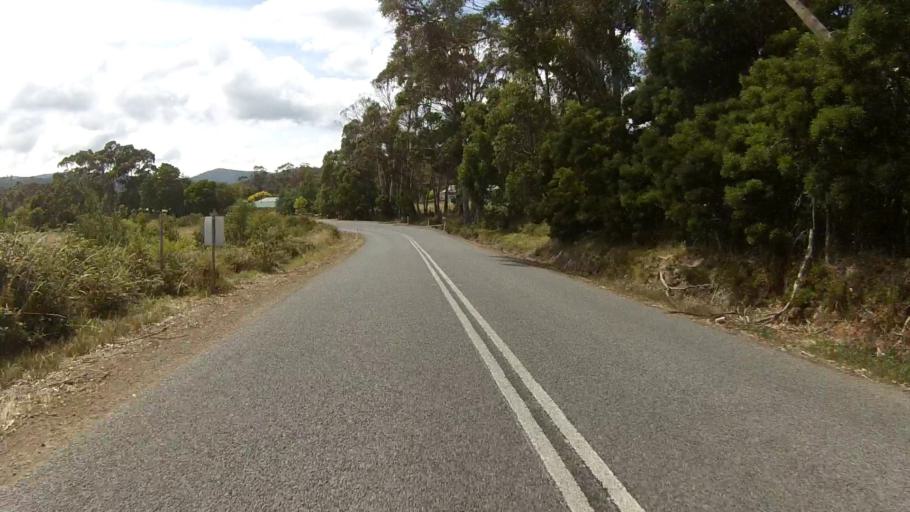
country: AU
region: Tasmania
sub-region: Huon Valley
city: Cygnet
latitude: -43.1878
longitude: 147.1015
